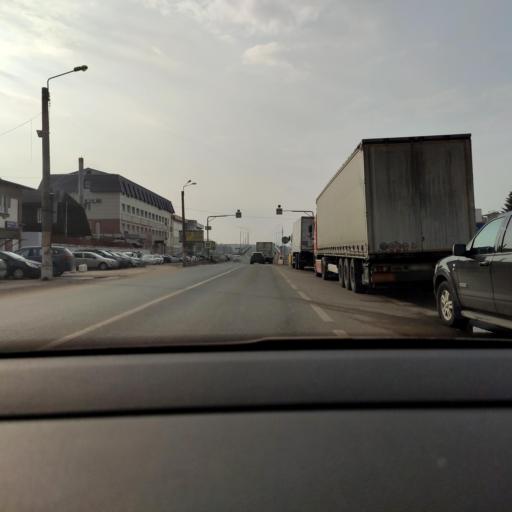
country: RU
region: Moskovskaya
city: Lesnyye Polyany
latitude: 55.9830
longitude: 37.8646
